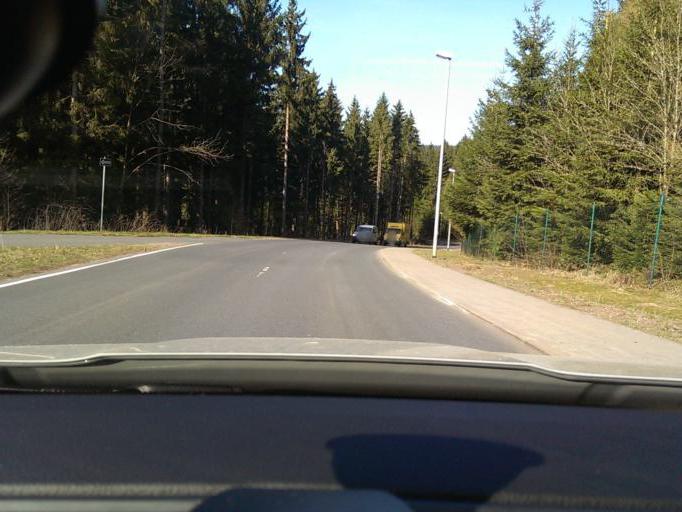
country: DE
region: Thuringia
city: Suhl
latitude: 50.5821
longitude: 10.7112
